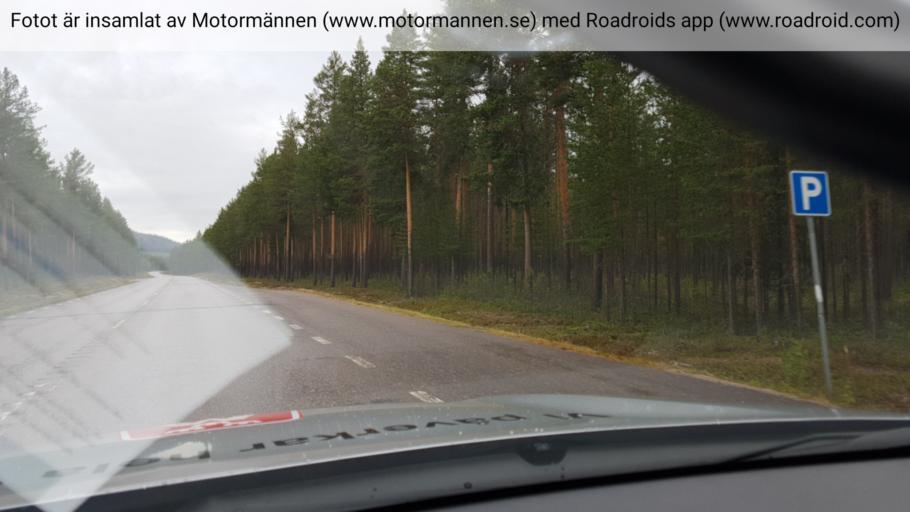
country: SE
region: Norrbotten
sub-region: Alvsbyns Kommun
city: AElvsbyn
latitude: 66.1360
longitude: 20.8959
